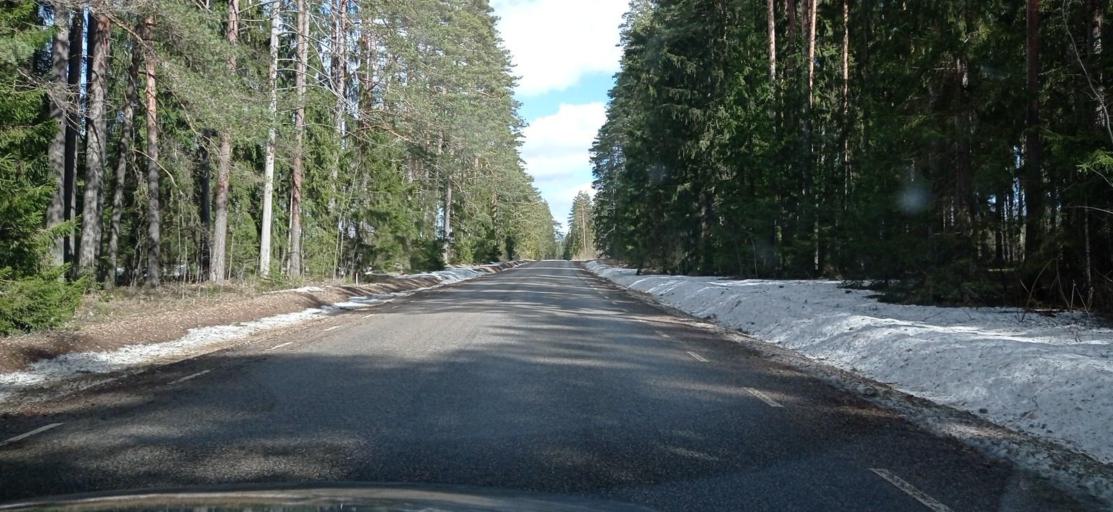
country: EE
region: Polvamaa
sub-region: Polva linn
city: Polva
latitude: 58.1511
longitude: 27.0462
